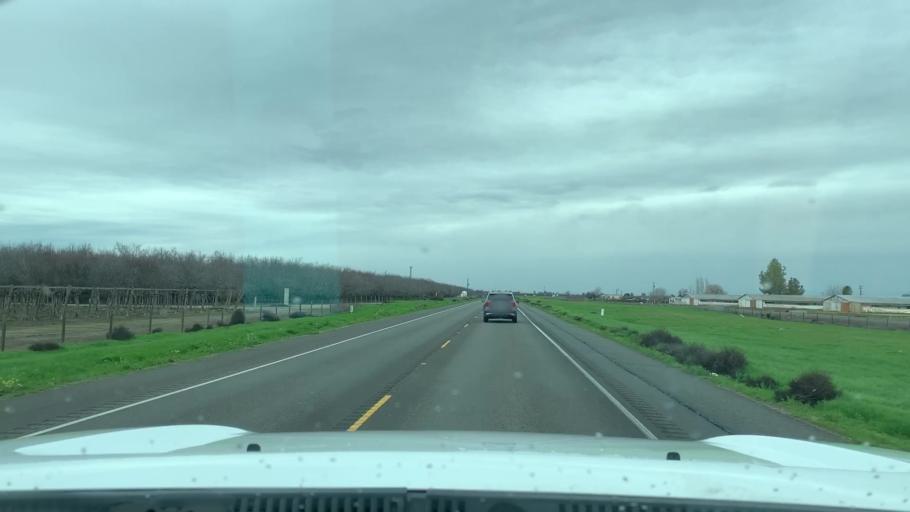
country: US
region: California
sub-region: Fresno County
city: Caruthers
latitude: 36.4777
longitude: -119.7929
